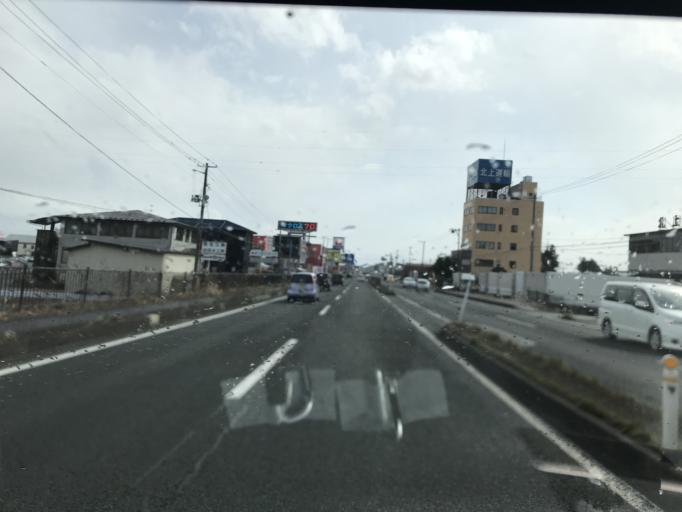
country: JP
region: Iwate
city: Kitakami
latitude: 39.3036
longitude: 141.1085
